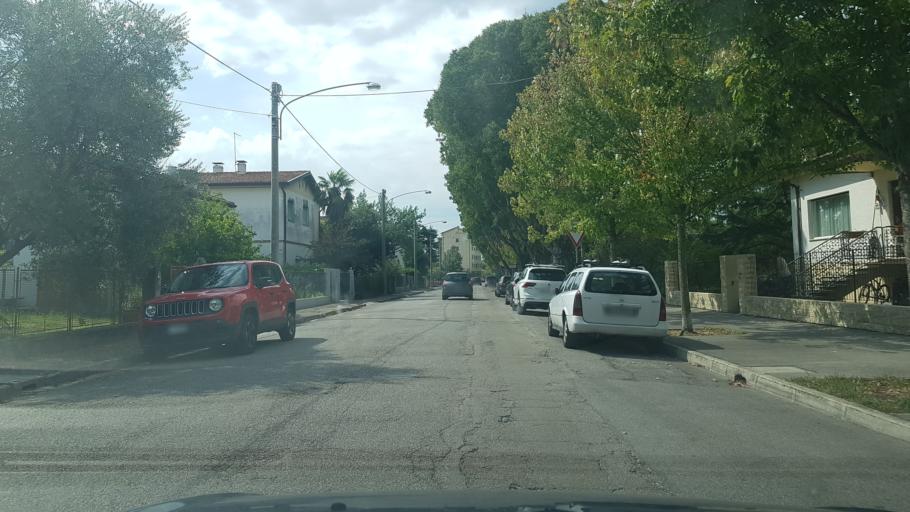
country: IT
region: Friuli Venezia Giulia
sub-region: Provincia di Gorizia
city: Gorizia
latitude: 45.9411
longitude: 13.6047
